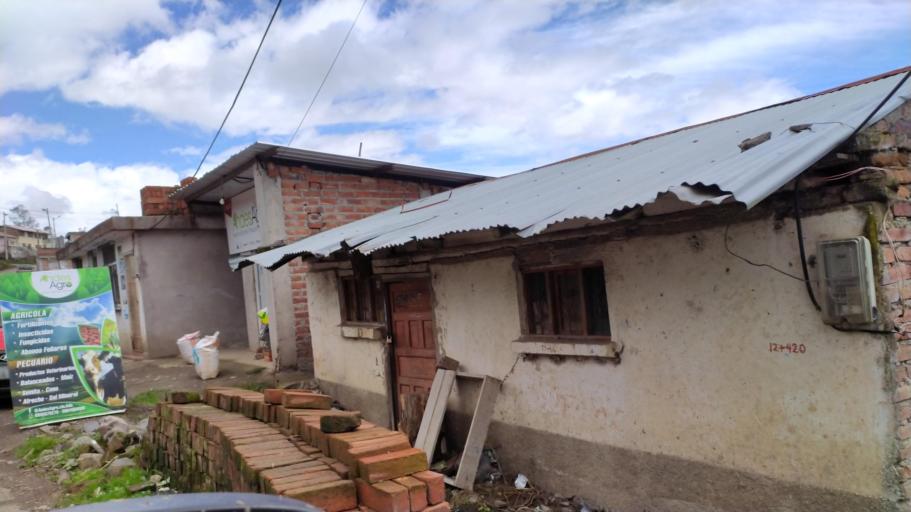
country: EC
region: Chimborazo
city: Riobamba
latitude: -1.6907
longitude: -78.5778
